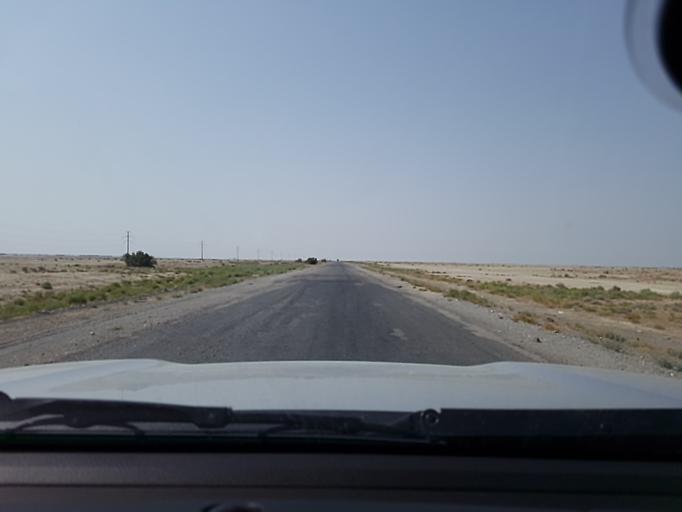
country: TM
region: Balkan
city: Gumdag
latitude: 38.8839
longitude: 54.5933
